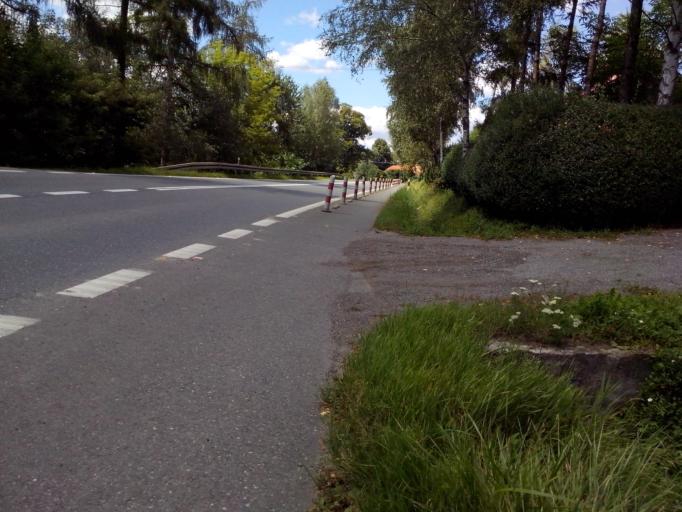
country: PL
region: Subcarpathian Voivodeship
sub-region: Powiat strzyzowski
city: Jawornik
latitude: 49.8054
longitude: 21.8944
